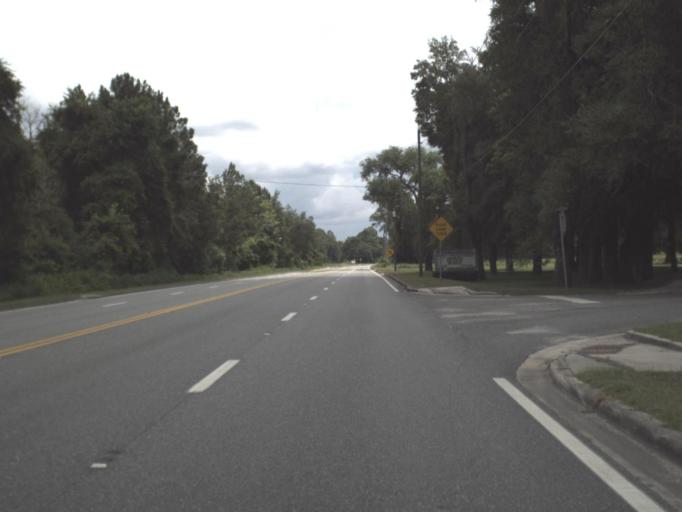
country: US
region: Florida
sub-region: Taylor County
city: Perry
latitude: 30.0907
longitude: -83.5363
